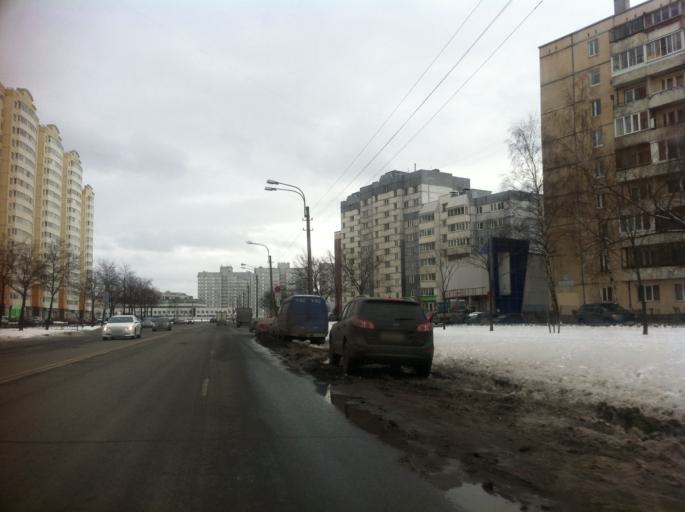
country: RU
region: St.-Petersburg
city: Uritsk
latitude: 59.8499
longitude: 30.2102
